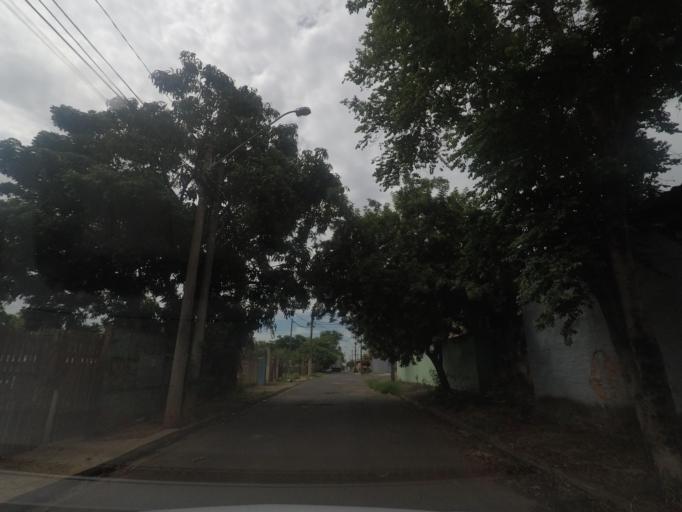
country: BR
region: Sao Paulo
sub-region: Nova Odessa
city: Nova Odessa
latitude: -22.8002
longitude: -47.2828
